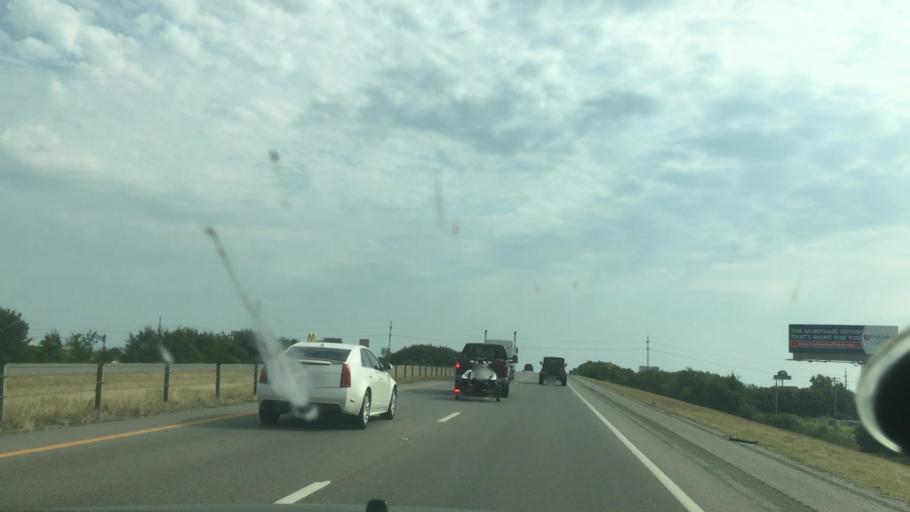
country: US
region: Oklahoma
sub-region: Bryan County
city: Durant
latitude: 33.9937
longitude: -96.4071
